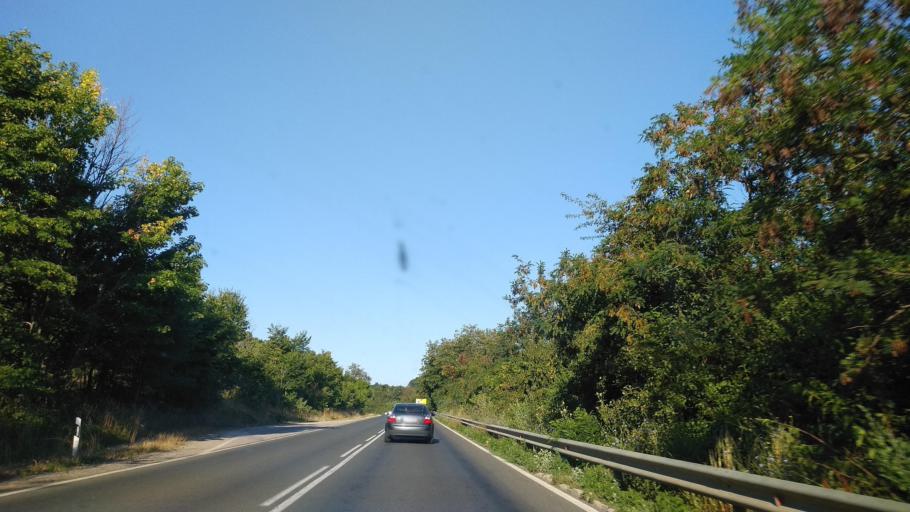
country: BG
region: Veliko Turnovo
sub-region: Obshtina Pavlikeni
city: Byala Cherkva
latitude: 43.0658
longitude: 25.2951
